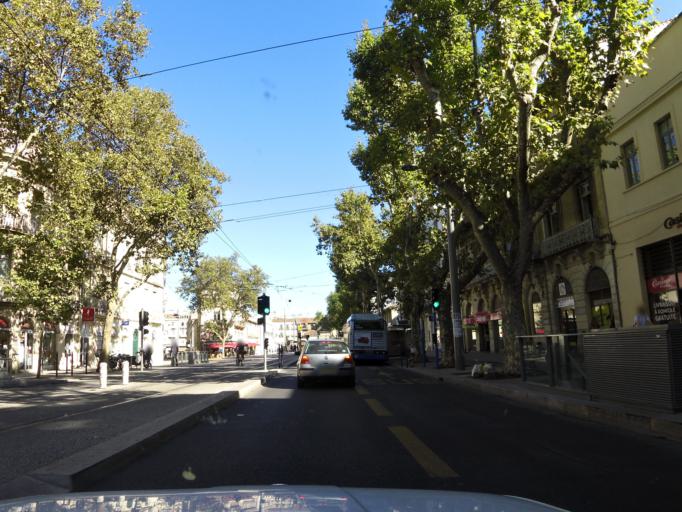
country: FR
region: Languedoc-Roussillon
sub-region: Departement de l'Herault
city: Montpellier
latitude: 43.6062
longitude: 3.8727
